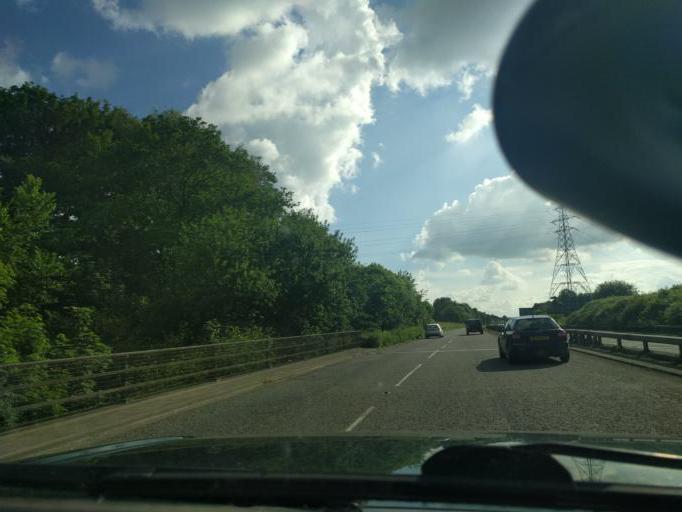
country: GB
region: England
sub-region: Bath and North East Somerset
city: Bath
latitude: 51.4022
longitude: -2.3107
